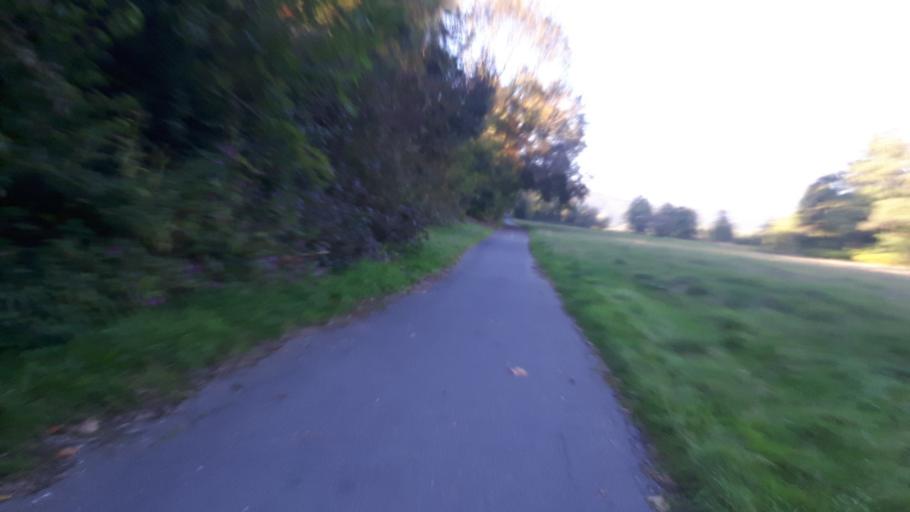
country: DE
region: Rheinland-Pfalz
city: Werkhausen
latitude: 50.7829
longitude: 7.5163
